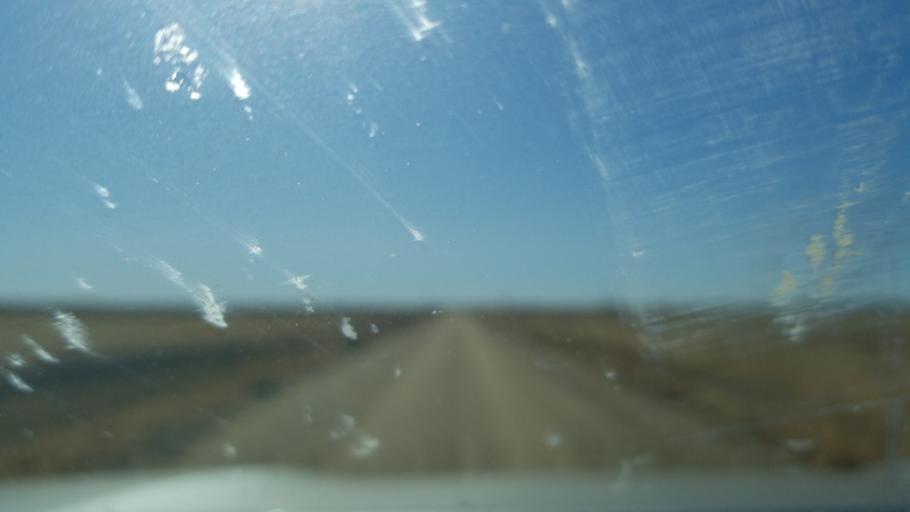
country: US
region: Kansas
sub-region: Ness County
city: Ness City
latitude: 38.5707
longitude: -99.6420
